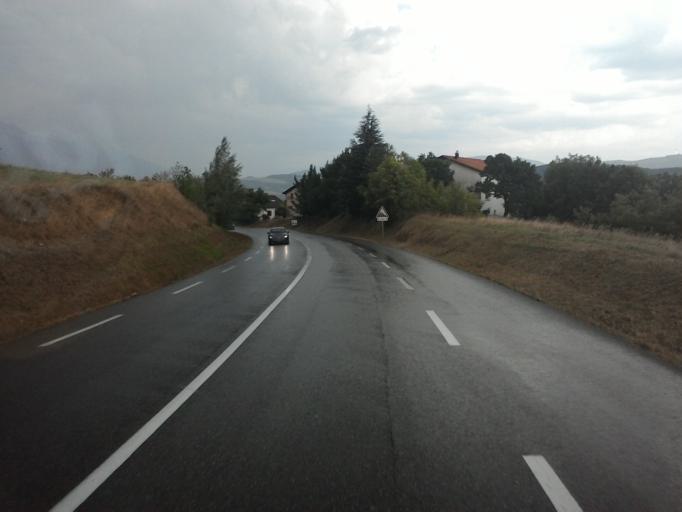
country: FR
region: Provence-Alpes-Cote d'Azur
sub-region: Departement des Hautes-Alpes
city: Gap
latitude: 44.5725
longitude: 6.0770
